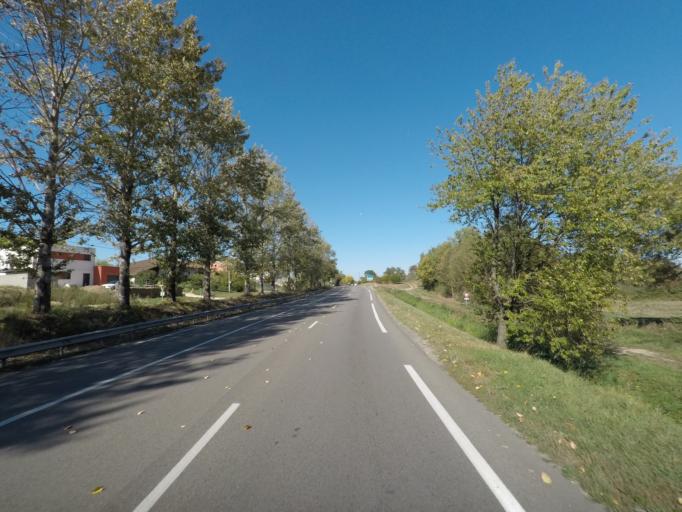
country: FR
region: Rhone-Alpes
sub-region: Departement de l'Ain
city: Viriat
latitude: 46.2346
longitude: 5.1985
